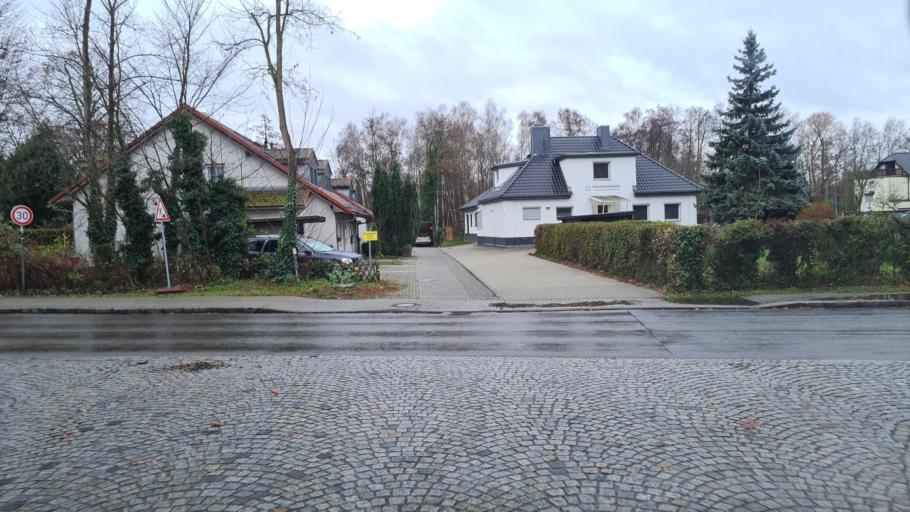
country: DE
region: Brandenburg
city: Luebben
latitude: 51.9408
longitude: 13.9006
